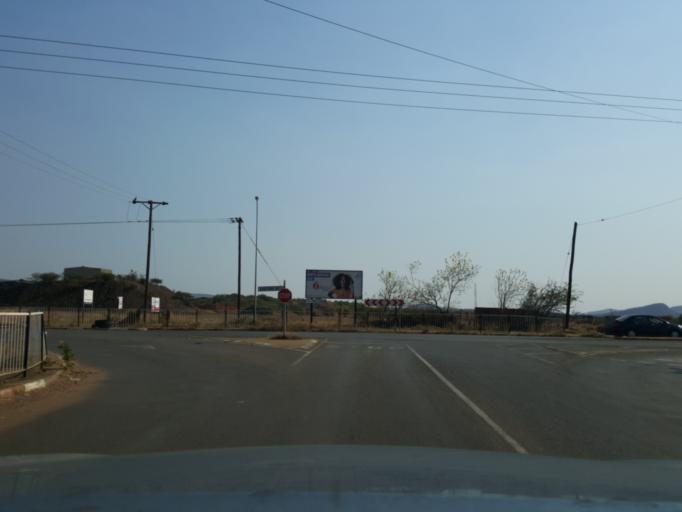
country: BW
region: South East
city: Lobatse
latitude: -25.2019
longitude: 25.6854
